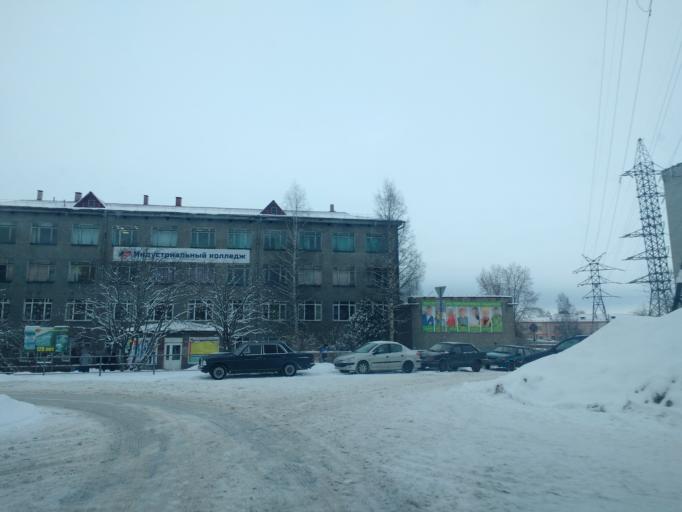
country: RU
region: Republic of Karelia
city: Petrozavodsk
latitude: 61.7958
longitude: 34.3556
